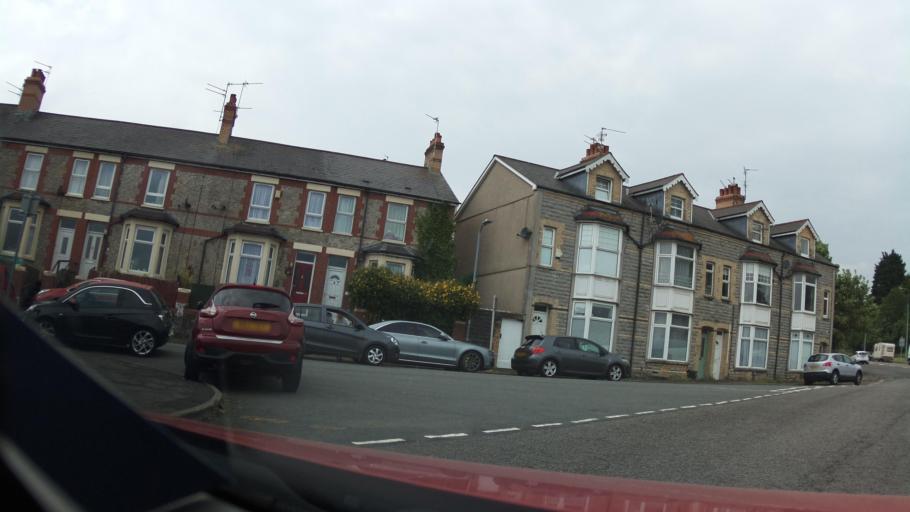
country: GB
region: Wales
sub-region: Vale of Glamorgan
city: Barry
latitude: 51.4109
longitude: -3.2536
